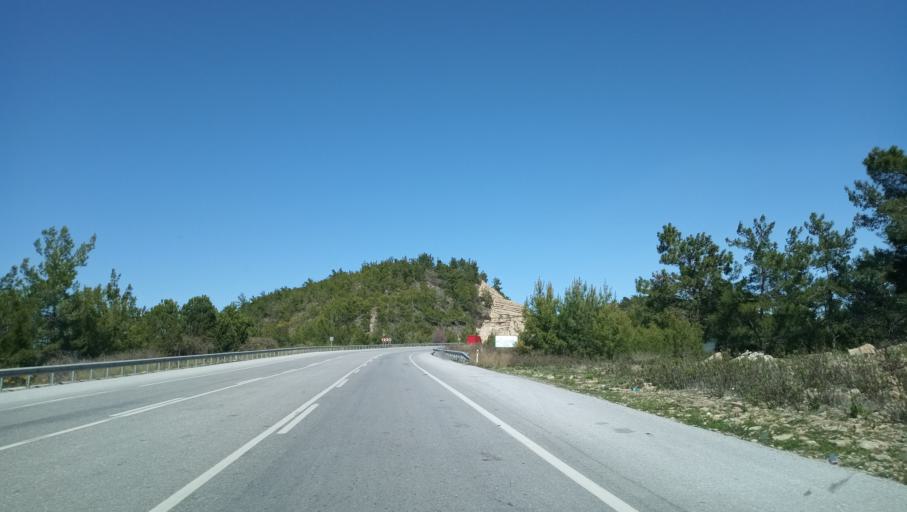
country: TR
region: Antalya
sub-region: Manavgat
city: Kizilagac
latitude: 36.7448
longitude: 31.6182
